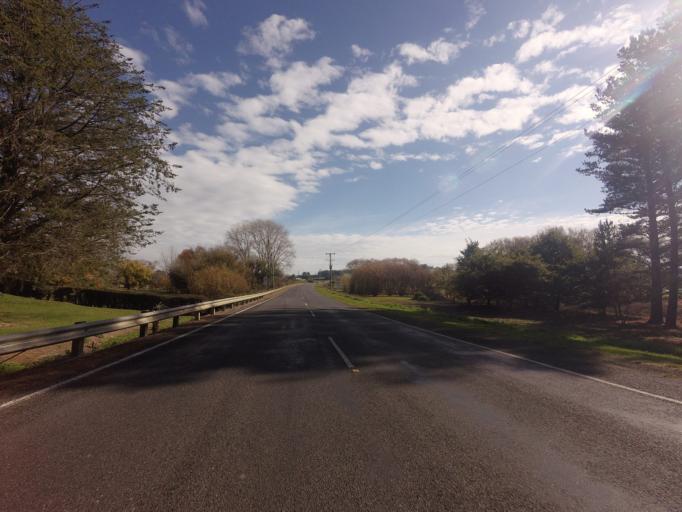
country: AU
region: Tasmania
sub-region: Meander Valley
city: Westbury
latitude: -41.5261
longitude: 146.8300
